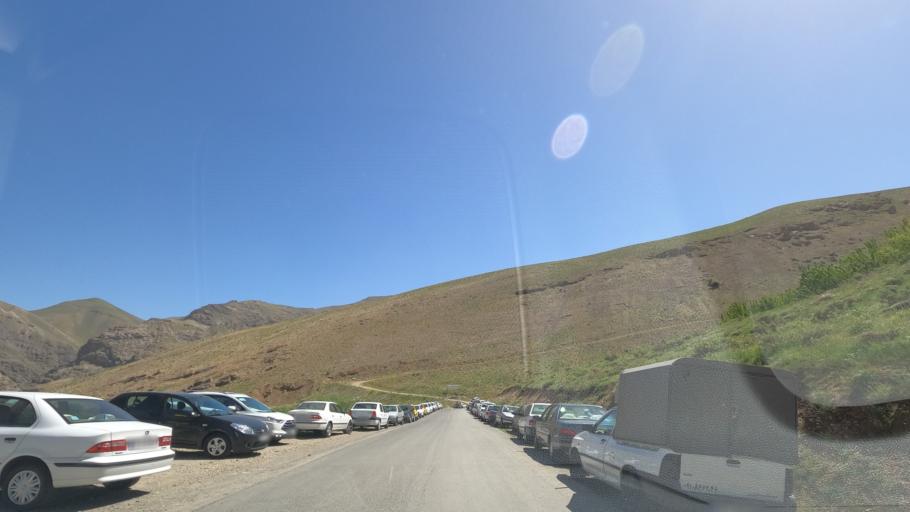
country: IR
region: Alborz
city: Karaj
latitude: 35.9217
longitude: 51.1614
